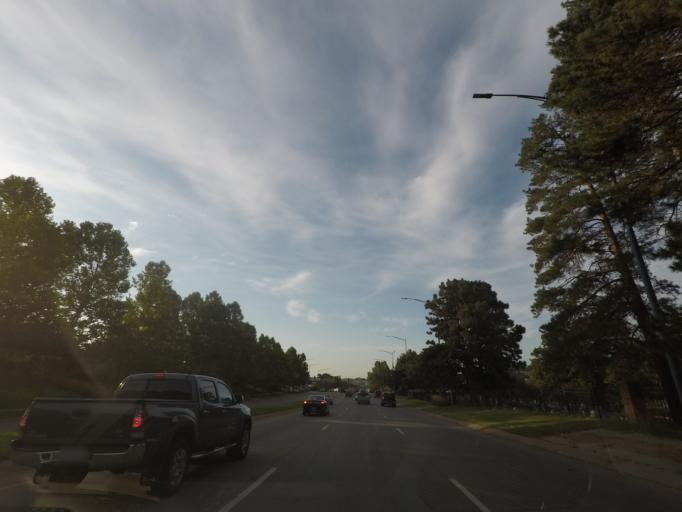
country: US
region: Iowa
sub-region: Polk County
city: Des Moines
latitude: 41.5897
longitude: -93.6449
